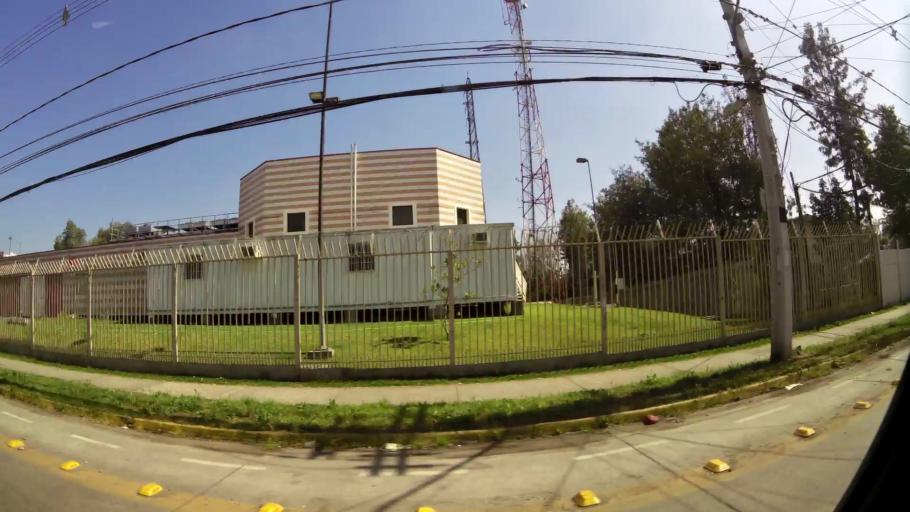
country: CL
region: Santiago Metropolitan
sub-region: Provincia de Santiago
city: Santiago
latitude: -33.4254
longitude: -70.6686
